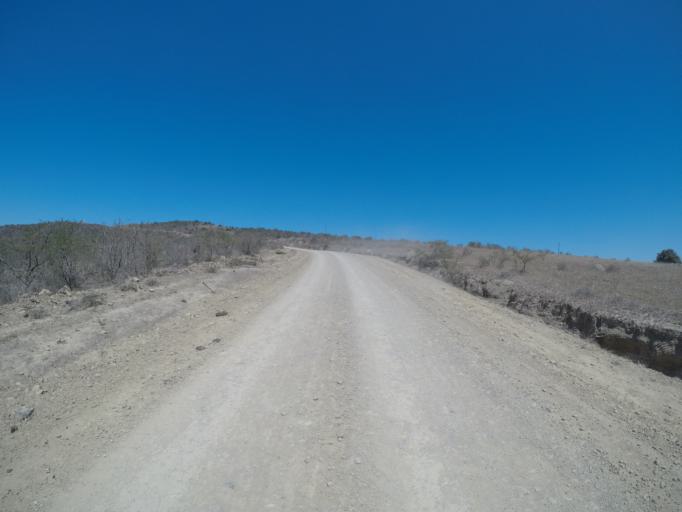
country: ZA
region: Eastern Cape
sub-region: OR Tambo District Municipality
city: Mthatha
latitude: -31.8749
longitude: 28.8725
